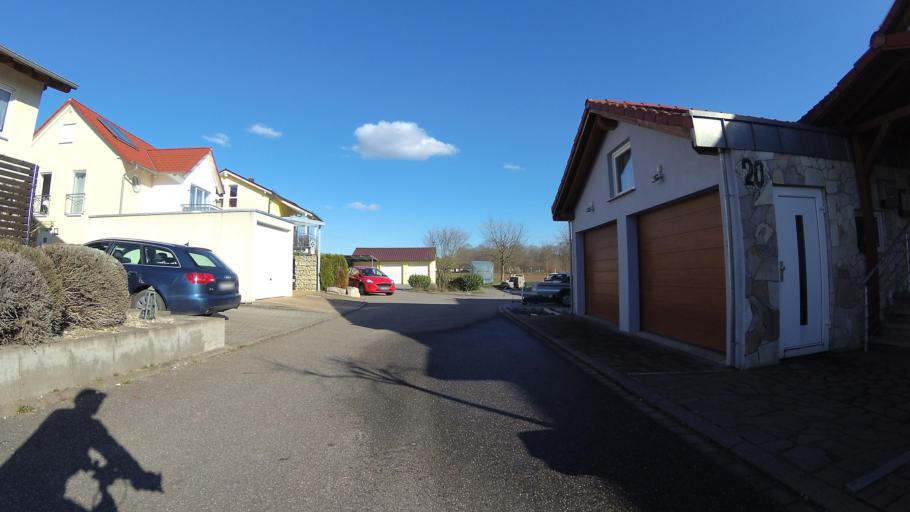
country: DE
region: Baden-Wuerttemberg
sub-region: Regierungsbezirk Stuttgart
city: Untereisesheim
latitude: 49.2394
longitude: 9.2025
